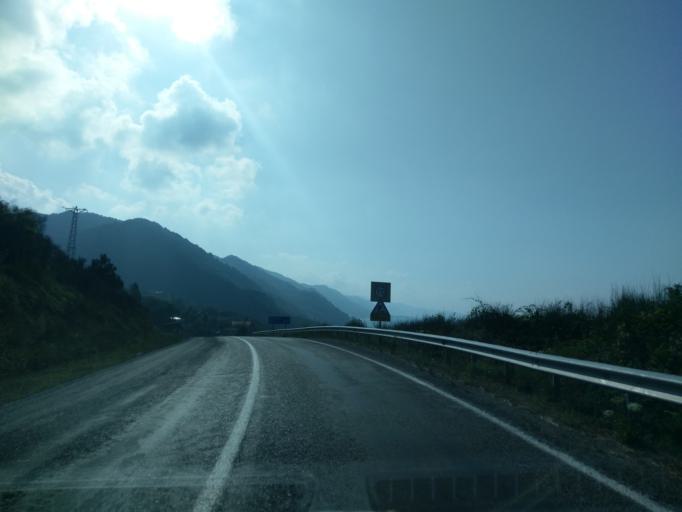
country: TR
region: Sinop
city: Ayancik
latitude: 41.9409
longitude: 34.6680
